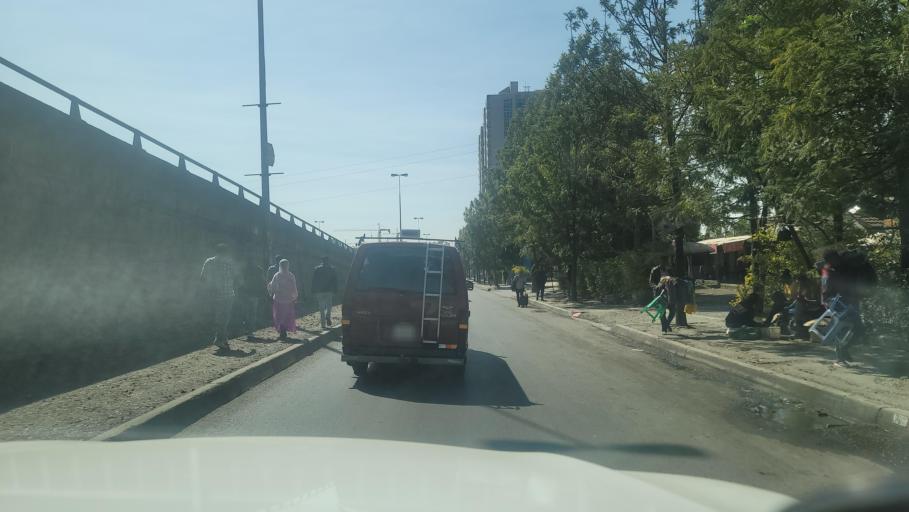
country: ET
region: Adis Abeba
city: Addis Ababa
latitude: 9.0172
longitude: 38.8022
